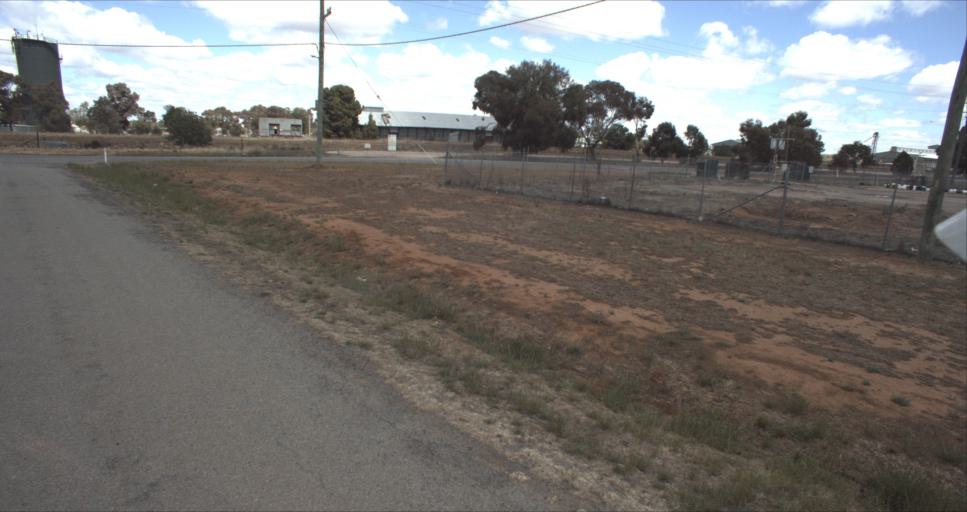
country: AU
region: New South Wales
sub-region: Murrumbidgee Shire
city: Darlington Point
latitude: -34.5150
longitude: 146.1826
